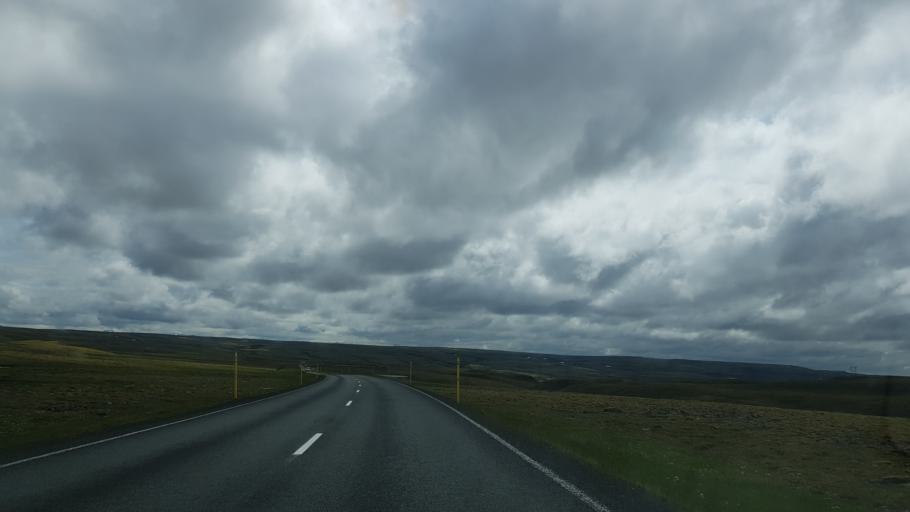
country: IS
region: West
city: Borgarnes
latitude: 64.9584
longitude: -21.0603
